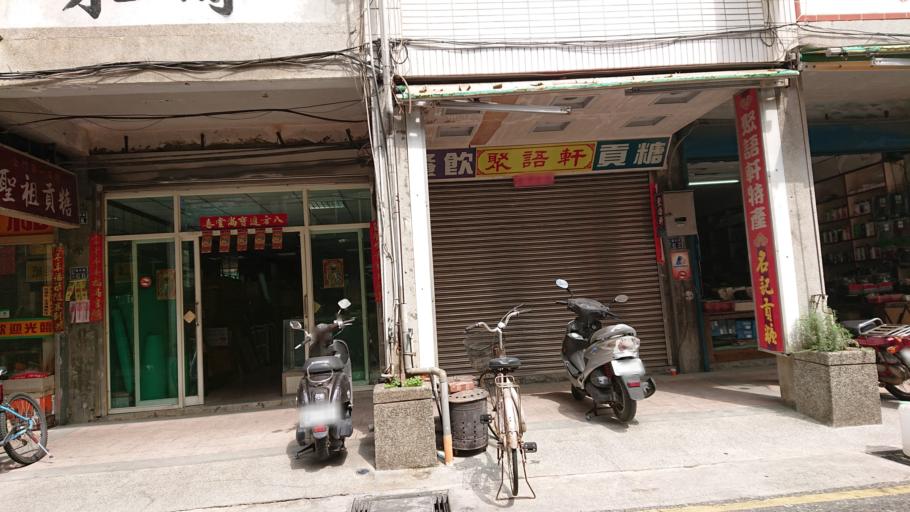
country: TW
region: Fukien
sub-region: Kinmen
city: Jincheng
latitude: 24.4417
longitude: 118.4154
